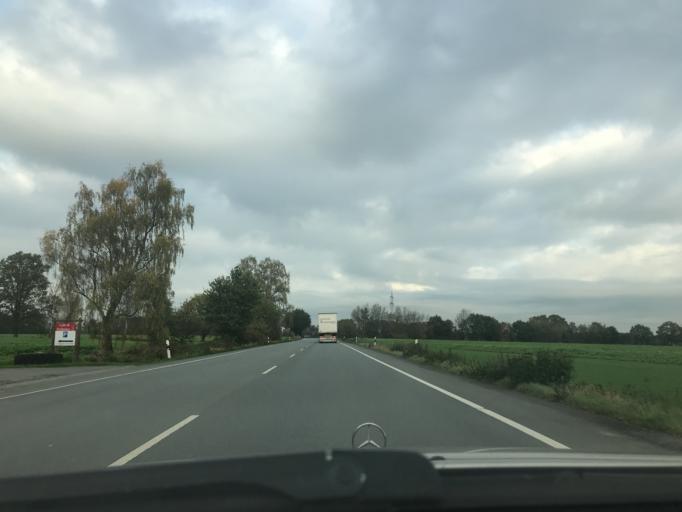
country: DE
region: North Rhine-Westphalia
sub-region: Regierungsbezirk Arnsberg
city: Welver
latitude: 51.6759
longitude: 8.0064
